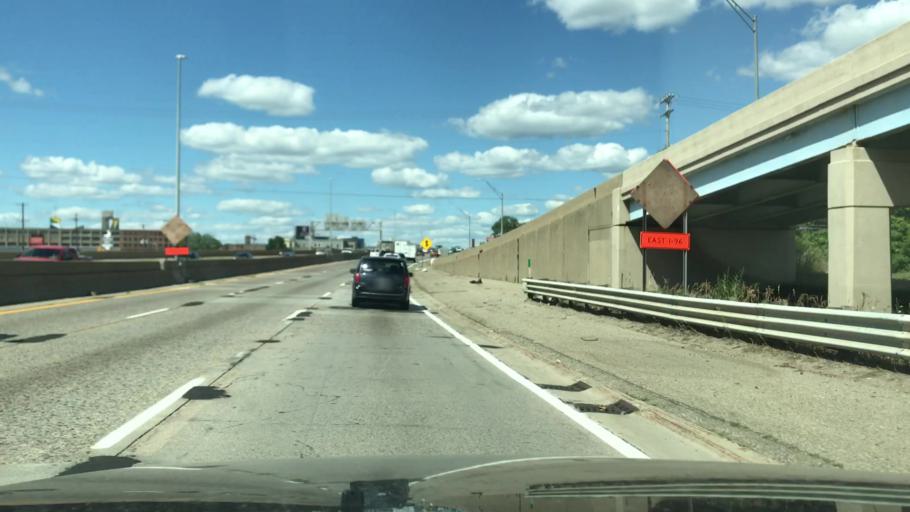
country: US
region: Michigan
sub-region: Kent County
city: Grand Rapids
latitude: 42.9495
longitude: -85.6743
